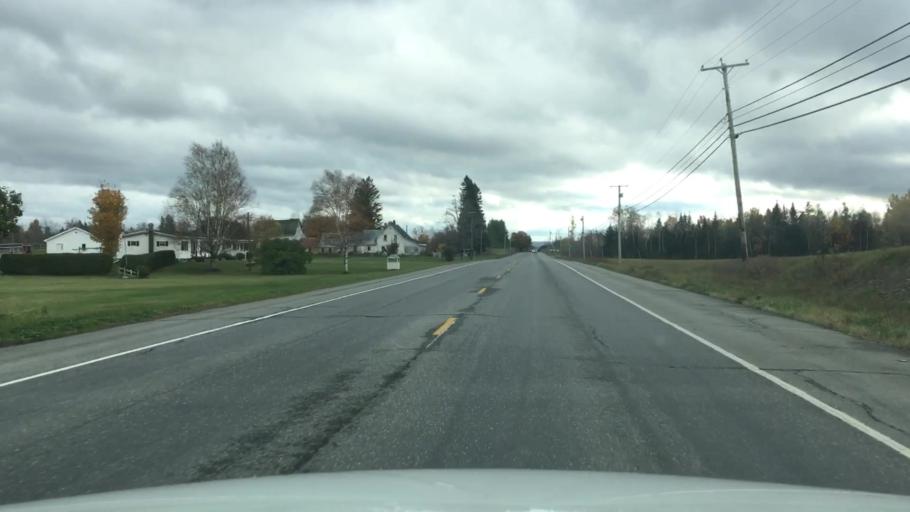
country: US
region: Maine
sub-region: Aroostook County
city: Houlton
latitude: 46.1870
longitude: -67.8412
